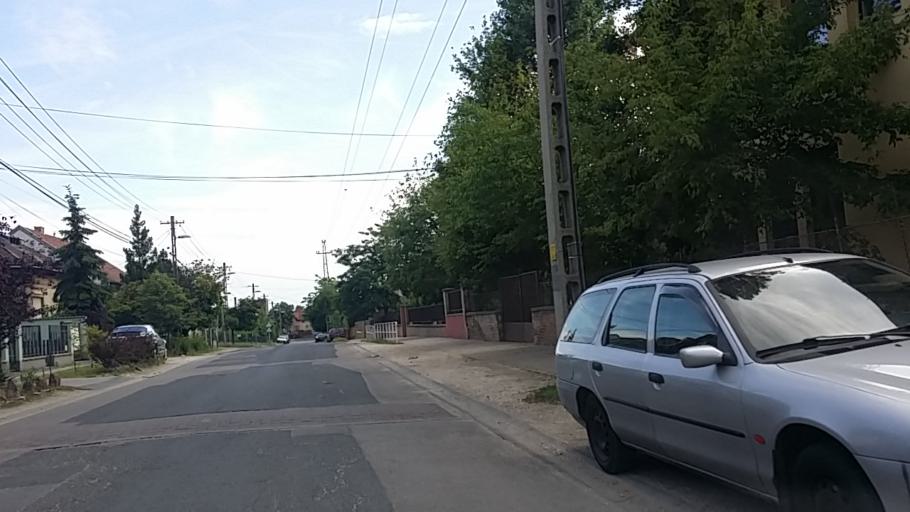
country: HU
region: Budapest
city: Budapest XXI. keruelet
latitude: 47.4191
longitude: 19.0777
